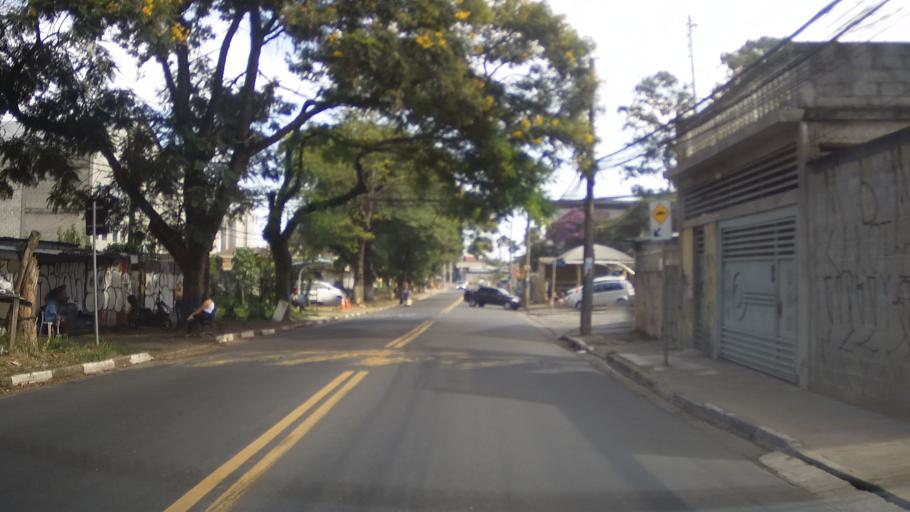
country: BR
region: Sao Paulo
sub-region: Guarulhos
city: Guarulhos
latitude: -23.4569
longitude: -46.5019
